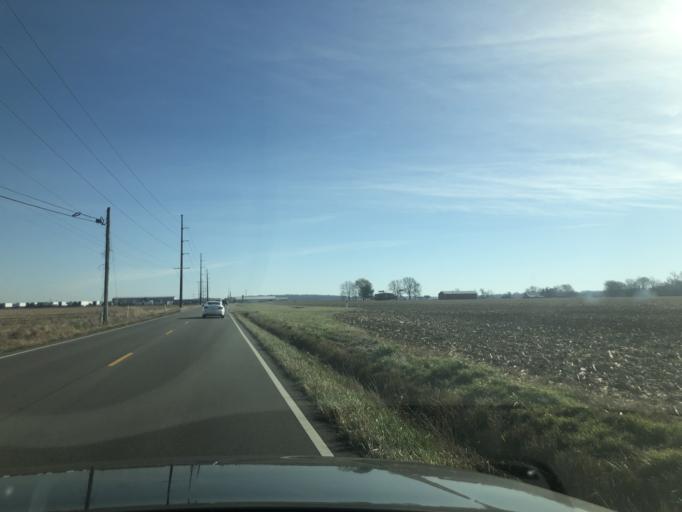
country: US
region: Indiana
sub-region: Warrick County
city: Newburgh
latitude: 37.9912
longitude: -87.4512
